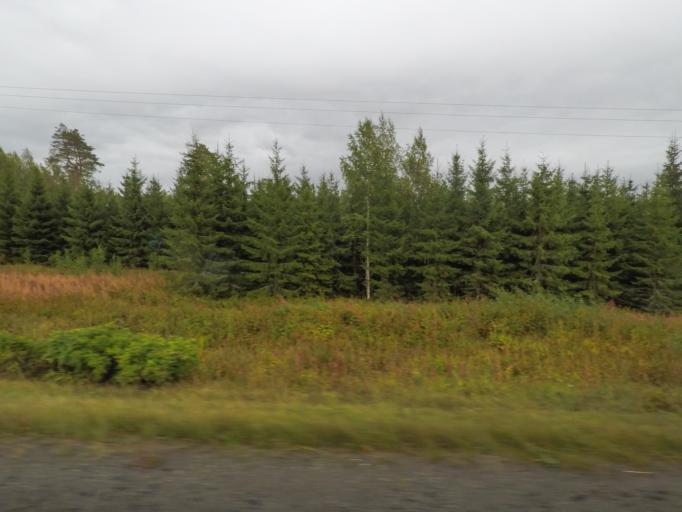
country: FI
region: Southern Savonia
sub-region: Pieksaemaeki
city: Juva
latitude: 61.9236
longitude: 27.8077
